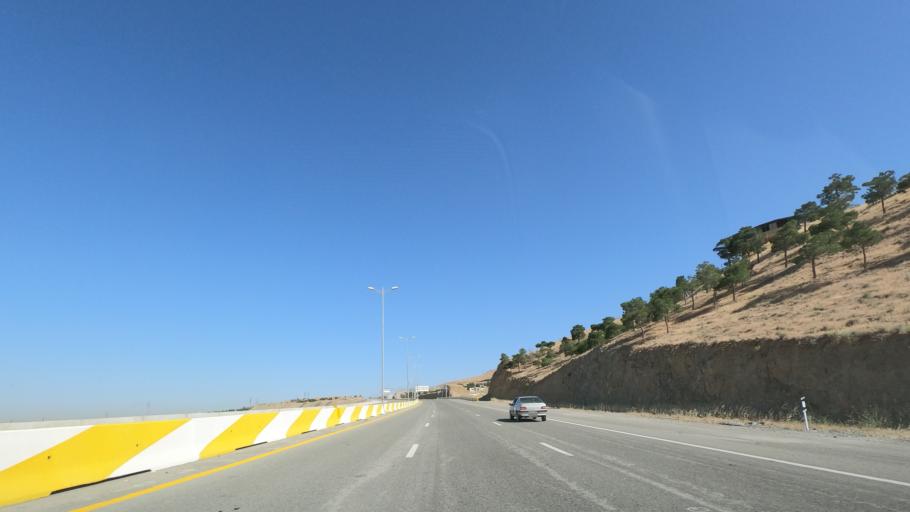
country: IR
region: Tehran
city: Shahr-e Qods
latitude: 35.7601
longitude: 51.0759
